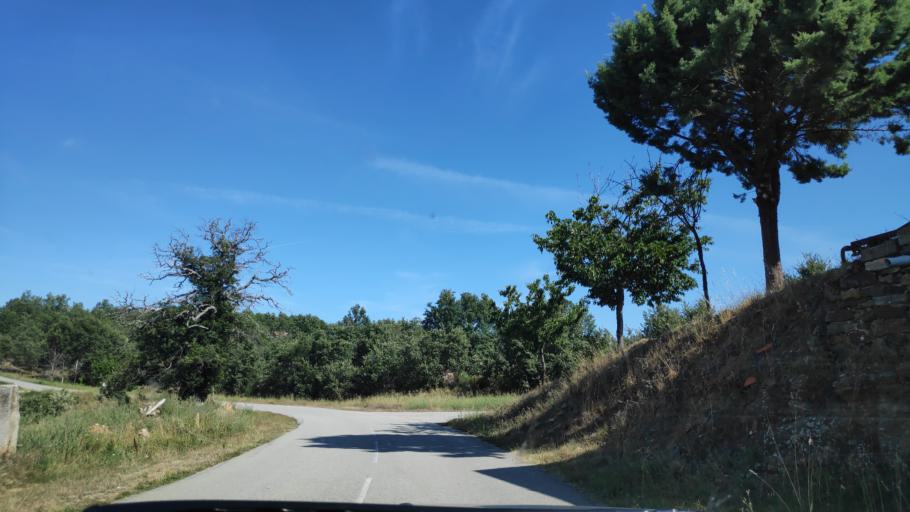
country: ES
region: Castille and Leon
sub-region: Provincia de Zamora
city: Alcanices
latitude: 41.6418
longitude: -6.3549
